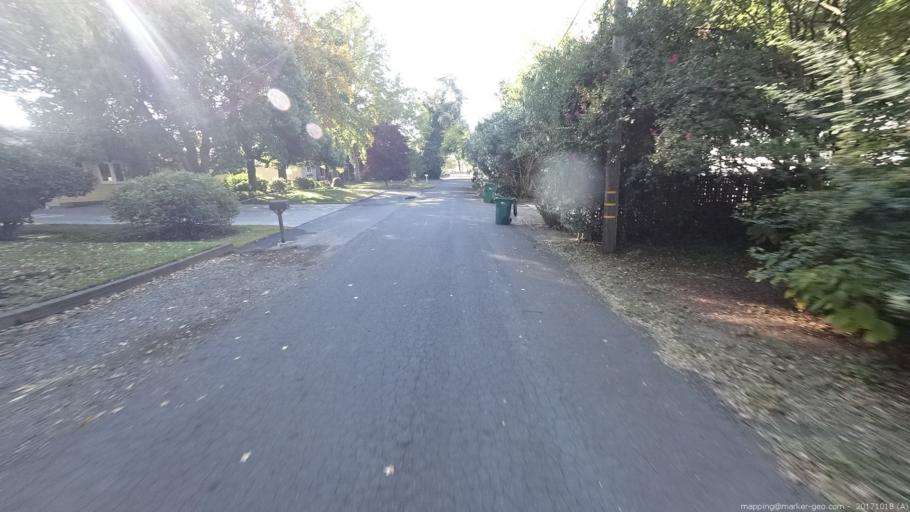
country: US
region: California
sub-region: Shasta County
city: Redding
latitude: 40.5629
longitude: -122.3687
